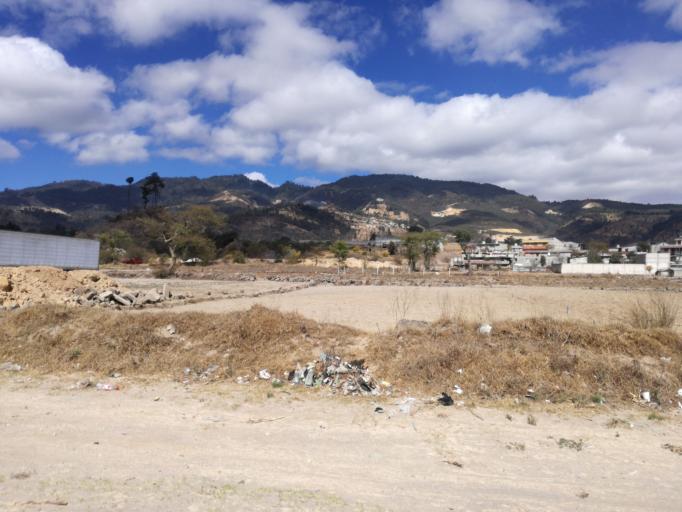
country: GT
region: Quetzaltenango
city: Quetzaltenango
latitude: 14.8087
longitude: -91.5403
